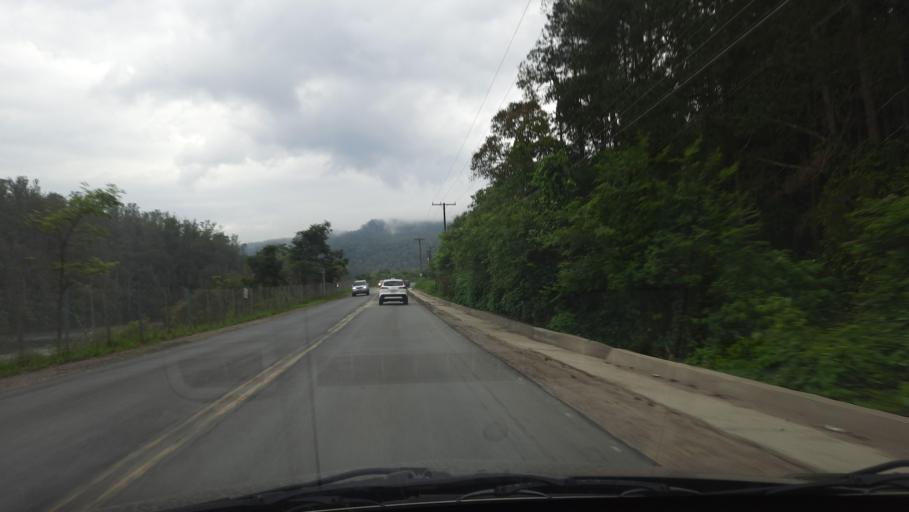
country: BR
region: Sao Paulo
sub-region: Franco Da Rocha
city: Franco da Rocha
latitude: -23.3434
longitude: -46.6617
